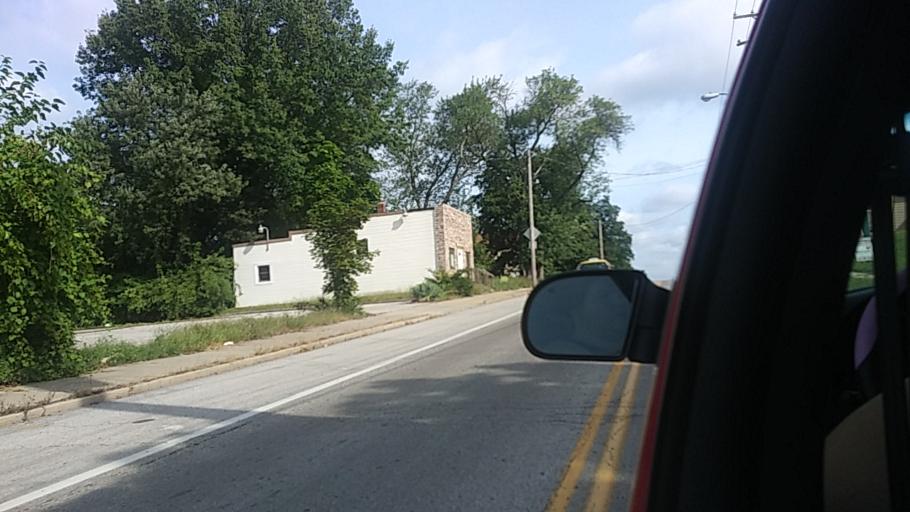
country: US
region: Ohio
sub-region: Summit County
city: Akron
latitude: 41.0811
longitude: -81.4904
